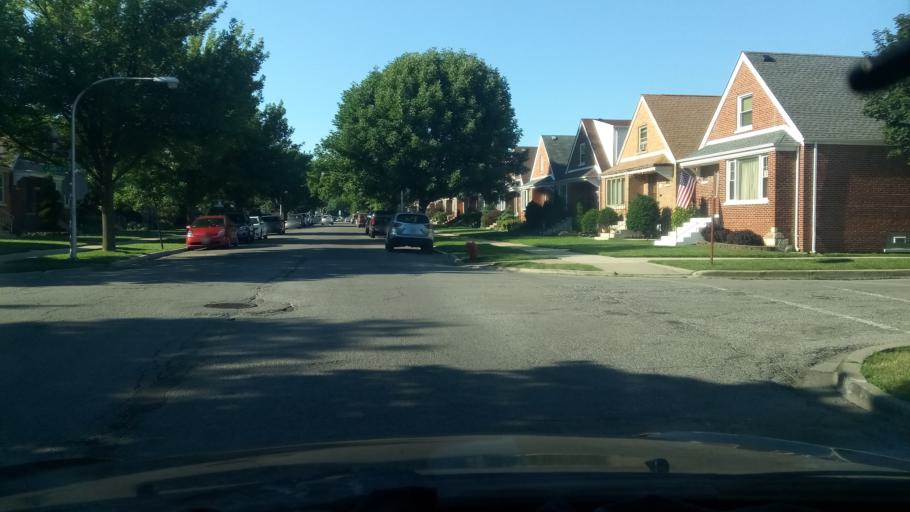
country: US
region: Illinois
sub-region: Cook County
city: Hometown
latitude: 41.7737
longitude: -87.7324
